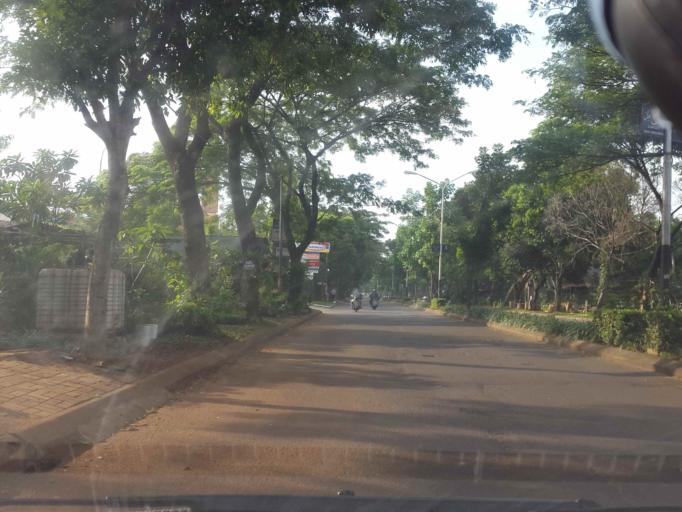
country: ID
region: Banten
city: South Tangerang
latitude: -6.2710
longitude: 106.6906
